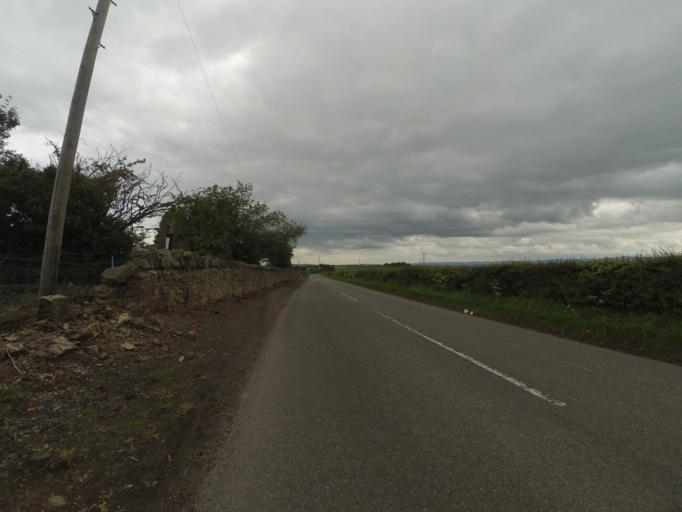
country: GB
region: Scotland
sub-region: East Lothian
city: Prestonpans
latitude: 55.9161
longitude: -2.9979
